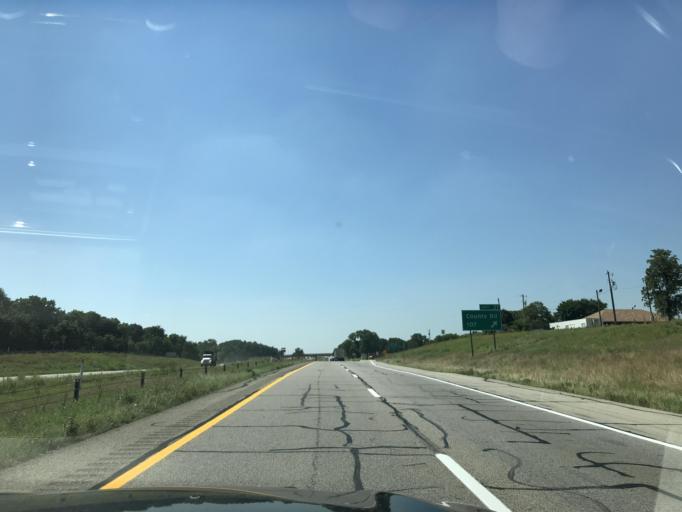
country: US
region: Texas
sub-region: Johnson County
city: Alvarado
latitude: 32.3584
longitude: -97.1984
